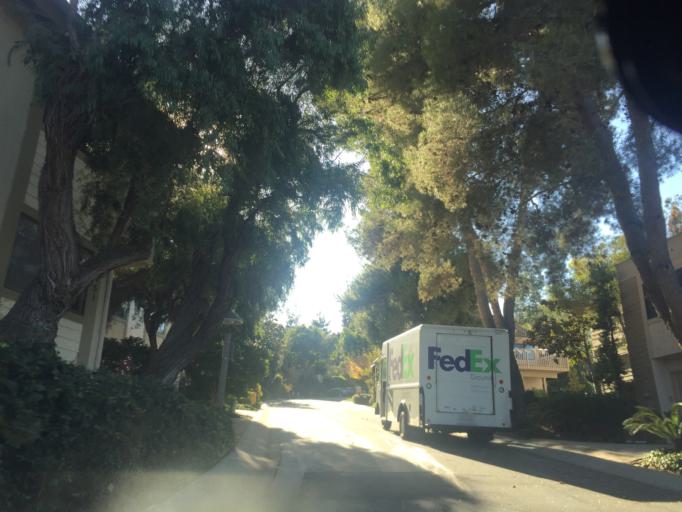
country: US
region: California
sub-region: San Diego County
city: Lemon Grove
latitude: 32.7738
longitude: -117.1010
